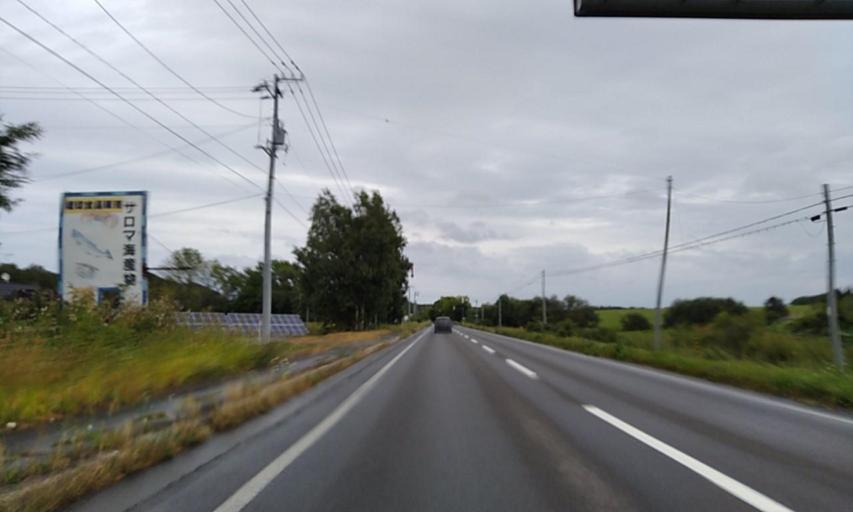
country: JP
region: Hokkaido
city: Kitami
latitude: 44.0869
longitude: 143.9519
